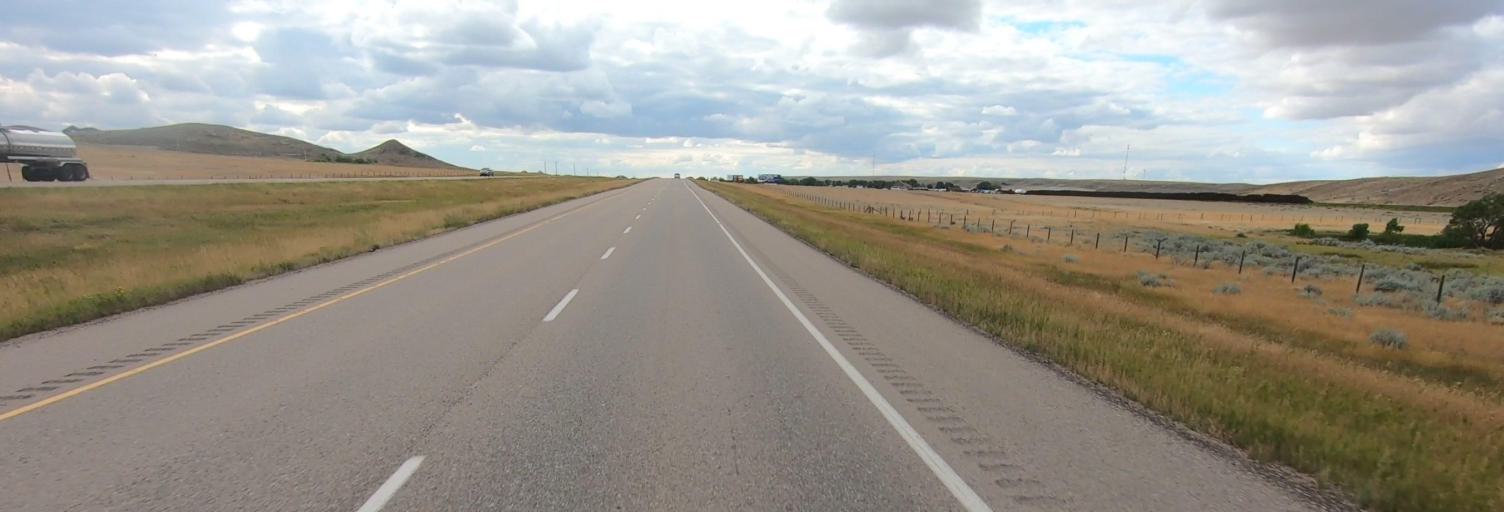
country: CA
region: Alberta
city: Medicine Hat
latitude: 49.9531
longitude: -110.2534
